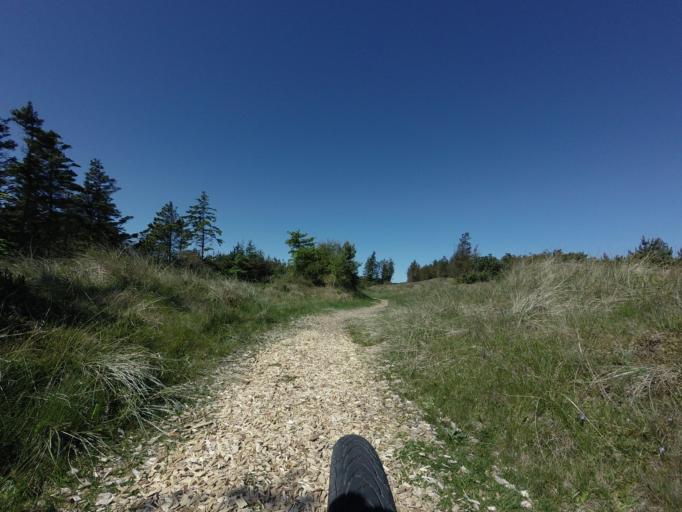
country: DK
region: North Denmark
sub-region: Jammerbugt Kommune
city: Pandrup
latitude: 57.3024
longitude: 9.6516
